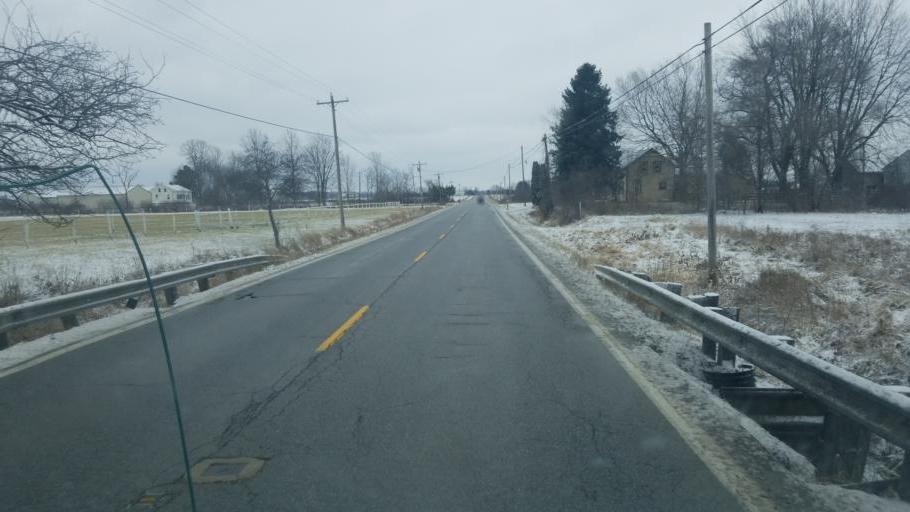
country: US
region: Ohio
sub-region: Licking County
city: Johnstown
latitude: 40.1957
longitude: -82.7654
